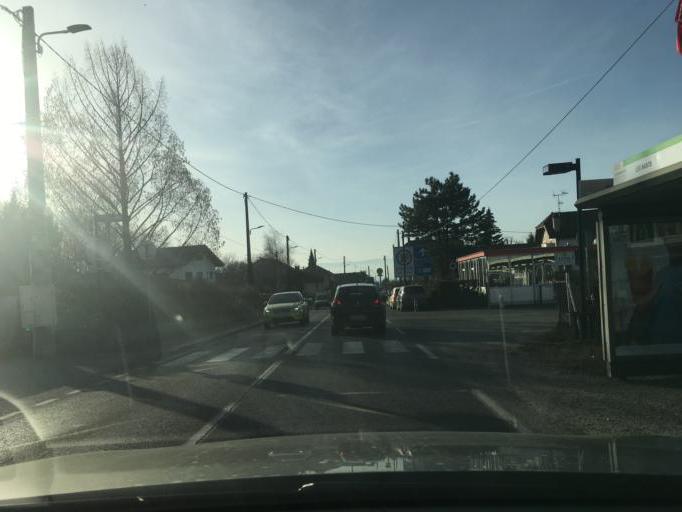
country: FR
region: Rhone-Alpes
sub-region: Departement de la Haute-Savoie
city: Ville-la-Grand
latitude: 46.1910
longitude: 6.2579
